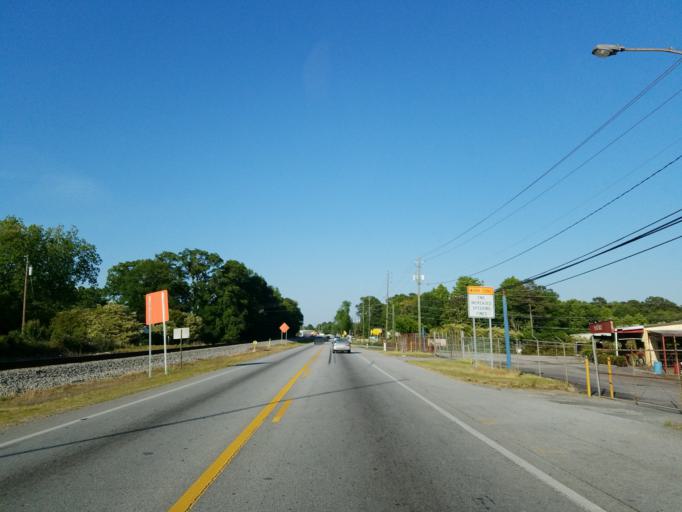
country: US
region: Georgia
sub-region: Douglas County
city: Douglasville
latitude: 33.7627
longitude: -84.7250
